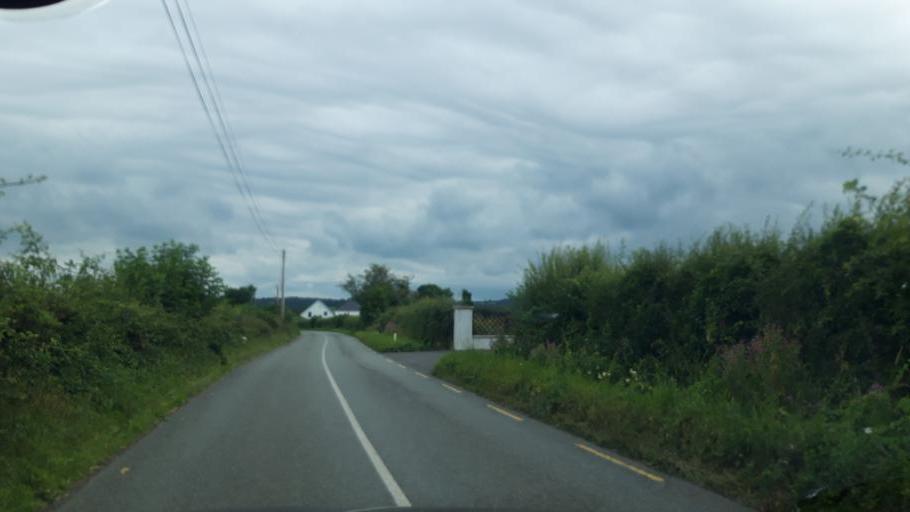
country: IE
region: Leinster
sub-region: Kilkenny
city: Ballyragget
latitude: 52.7416
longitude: -7.3986
